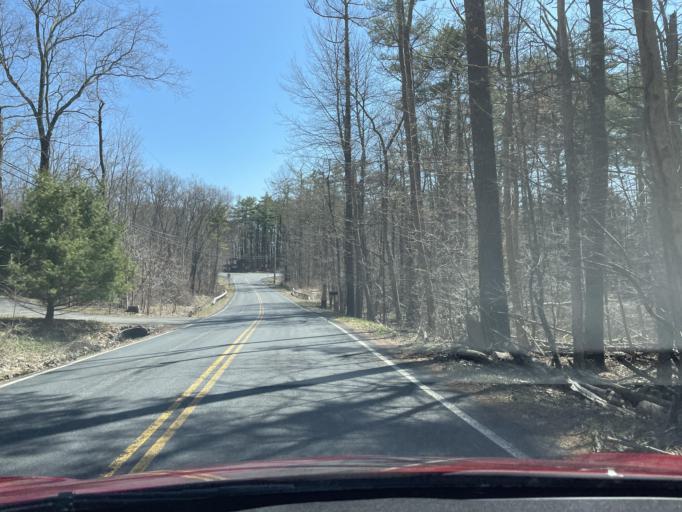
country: US
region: New York
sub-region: Ulster County
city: West Hurley
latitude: 42.0038
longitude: -74.1421
